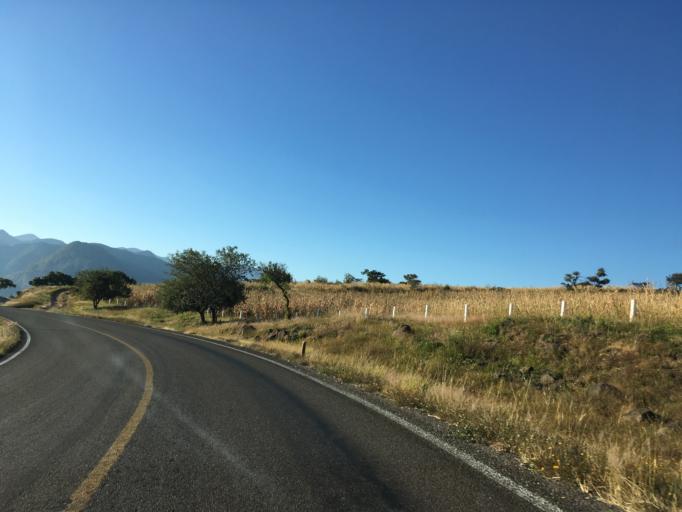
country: MX
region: Michoacan
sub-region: Tuxpan
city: La Soledad
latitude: 19.5050
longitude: -100.4655
